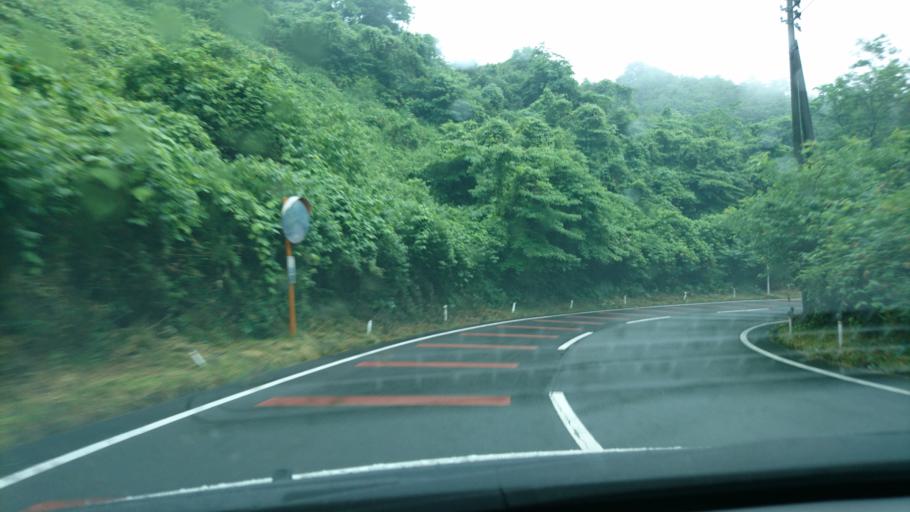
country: JP
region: Iwate
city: Ichinoseki
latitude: 38.8647
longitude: 141.0299
